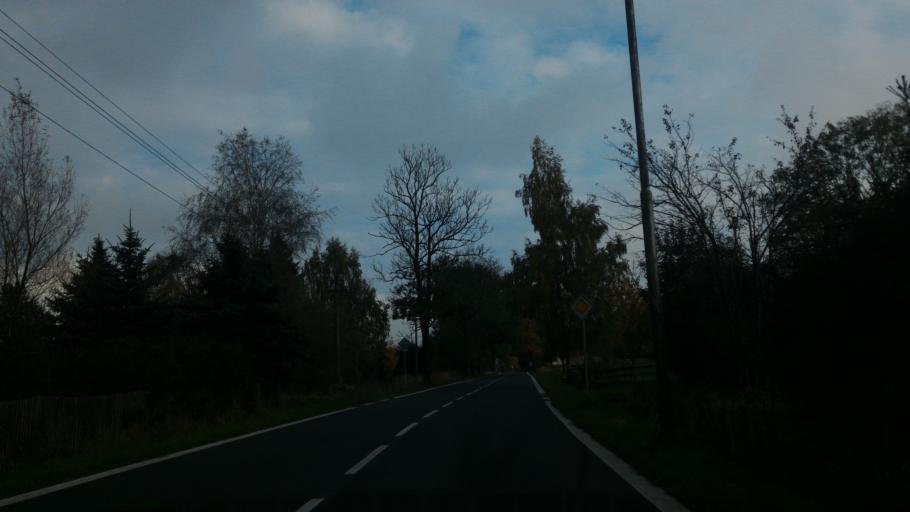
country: CZ
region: Ustecky
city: Dolni Podluzi
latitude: 50.8804
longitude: 14.5477
